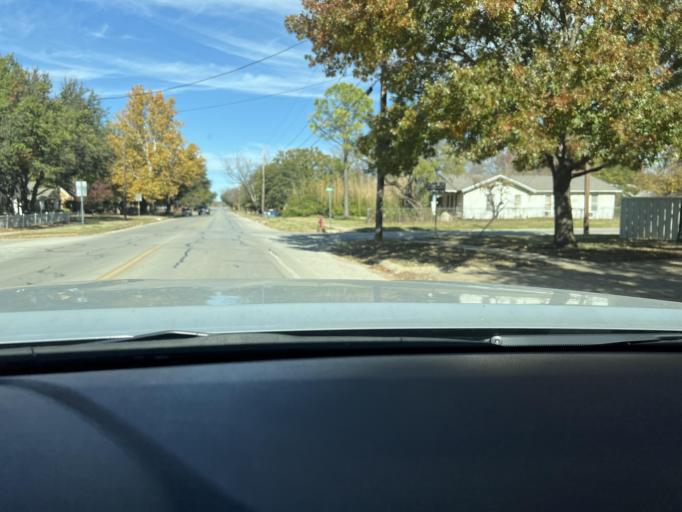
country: US
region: Texas
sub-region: Eastland County
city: Eastland
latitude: 32.3924
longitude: -98.8181
